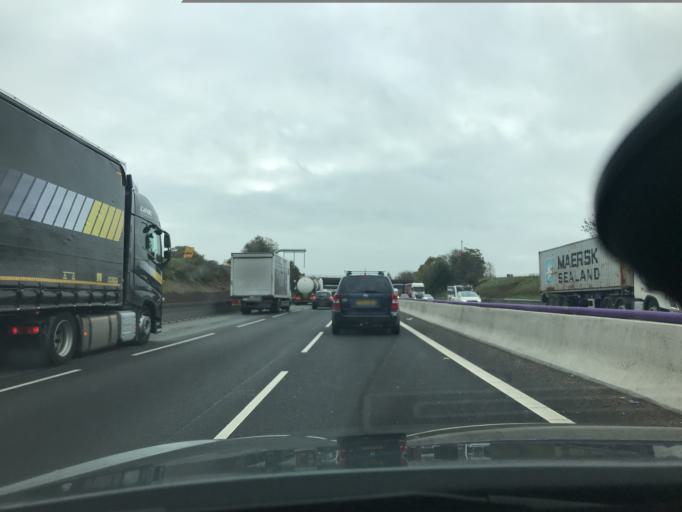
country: GB
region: England
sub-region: Cheshire East
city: Holmes Chapel
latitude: 53.2031
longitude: -2.3876
